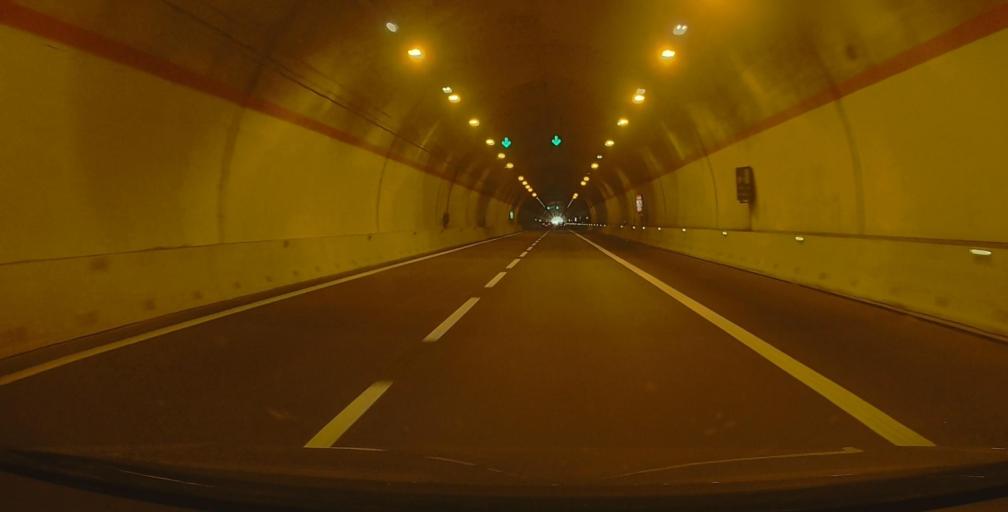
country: IT
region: Basilicate
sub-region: Provincia di Potenza
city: Lagonegro
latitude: 40.1459
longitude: 15.7531
